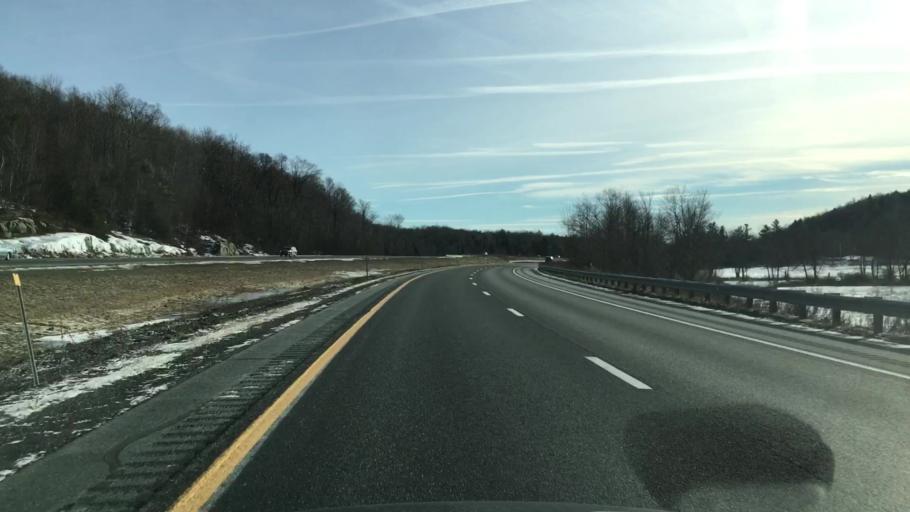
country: US
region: New Hampshire
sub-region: Sullivan County
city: Grantham
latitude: 43.5617
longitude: -72.1433
